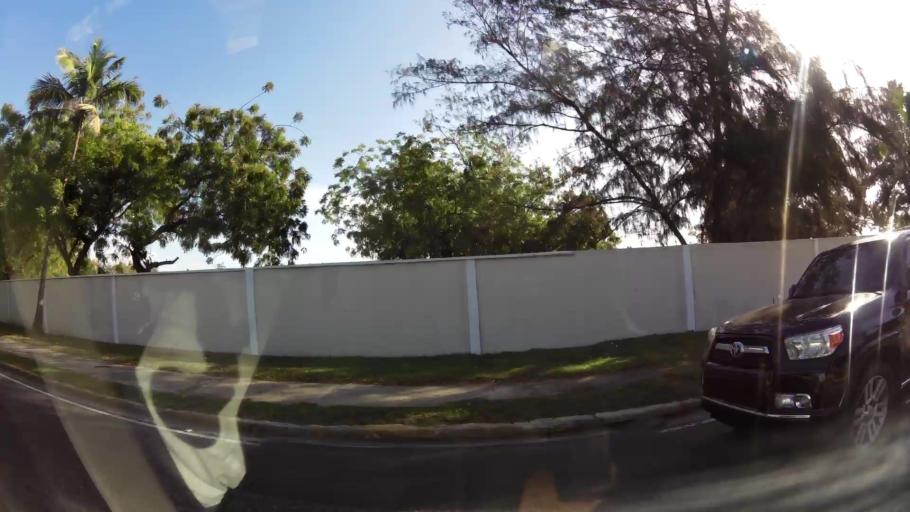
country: DO
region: Nacional
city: Ciudad Nueva
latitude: 18.4662
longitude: -69.8759
